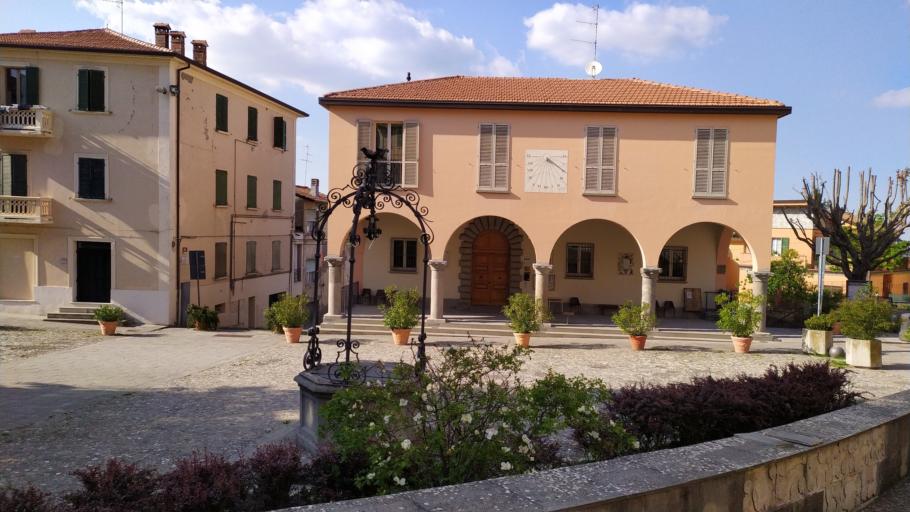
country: IT
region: Emilia-Romagna
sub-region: Provincia di Bologna
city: Borgo Tossignano
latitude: 44.2722
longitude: 11.6036
